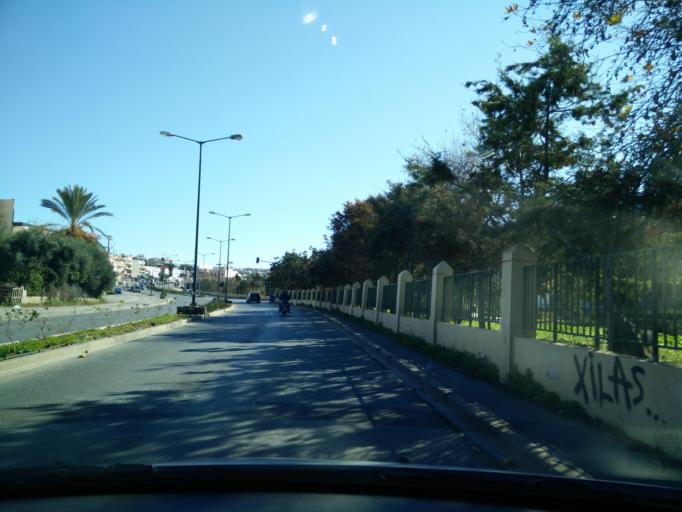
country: GR
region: Crete
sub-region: Nomos Irakleiou
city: Nea Alikarnassos
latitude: 35.3374
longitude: 25.1543
